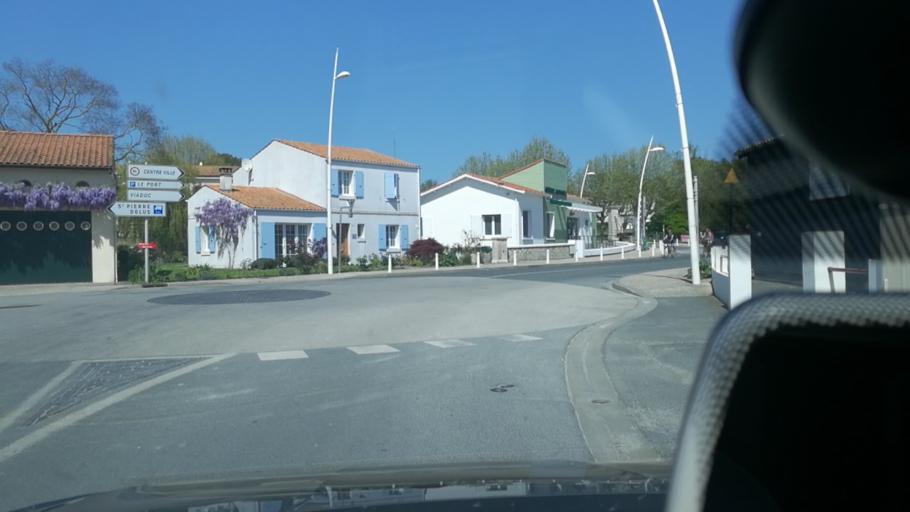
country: FR
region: Poitou-Charentes
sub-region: Departement de la Charente-Maritime
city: Saint-Trojan-les-Bains
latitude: 45.8838
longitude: -1.1958
